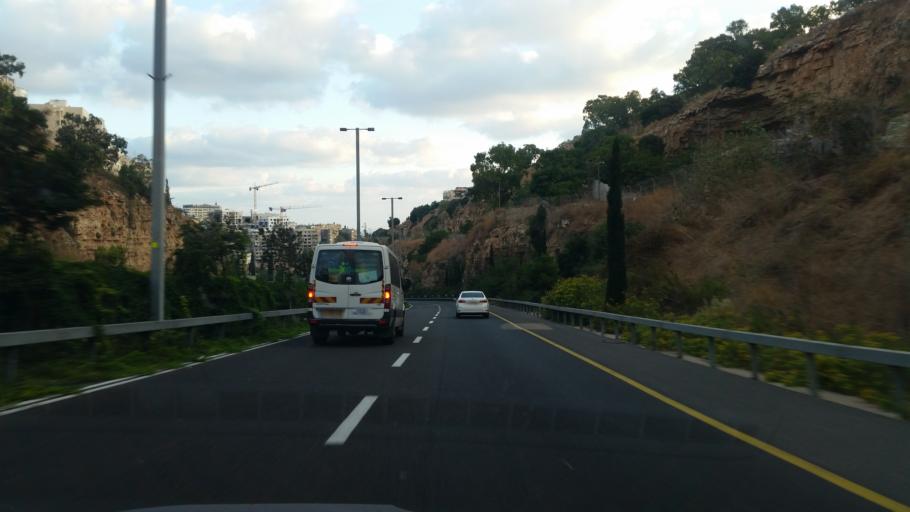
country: IL
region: Haifa
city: Haifa
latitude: 32.7969
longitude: 35.0049
